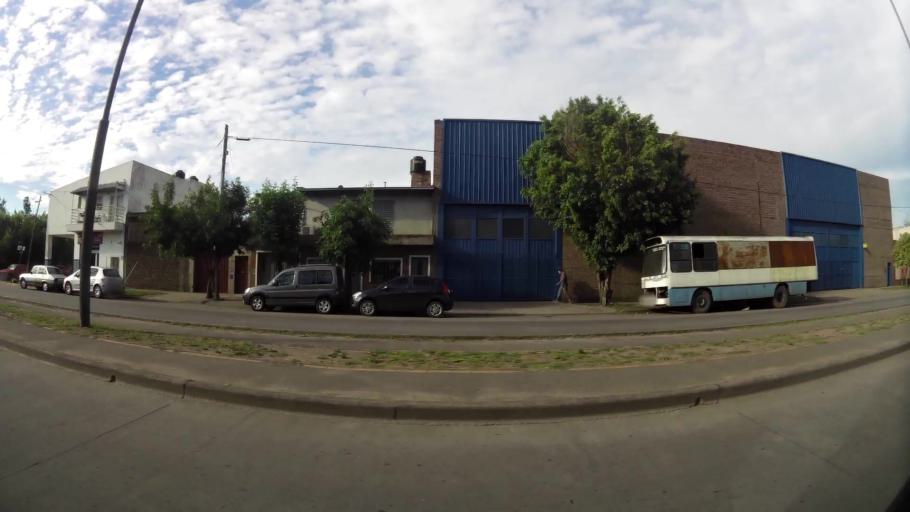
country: AR
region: Santa Fe
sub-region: Departamento de Rosario
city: Rosario
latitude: -32.9738
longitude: -60.6759
